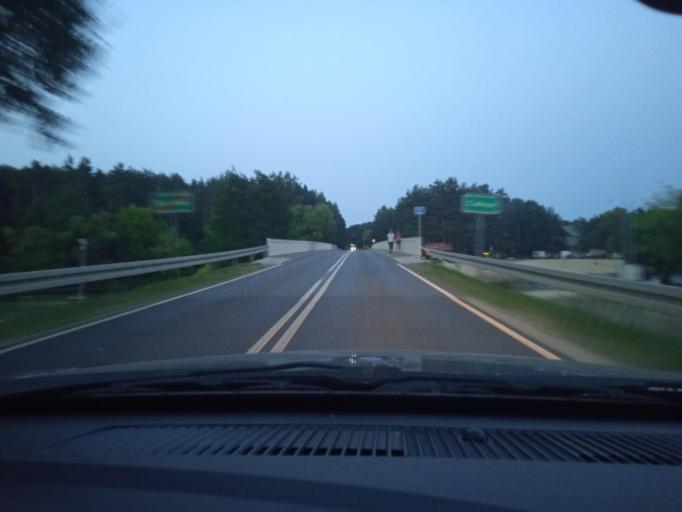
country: PL
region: Masovian Voivodeship
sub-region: Powiat plonski
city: Joniec
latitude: 52.5618
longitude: 20.6643
